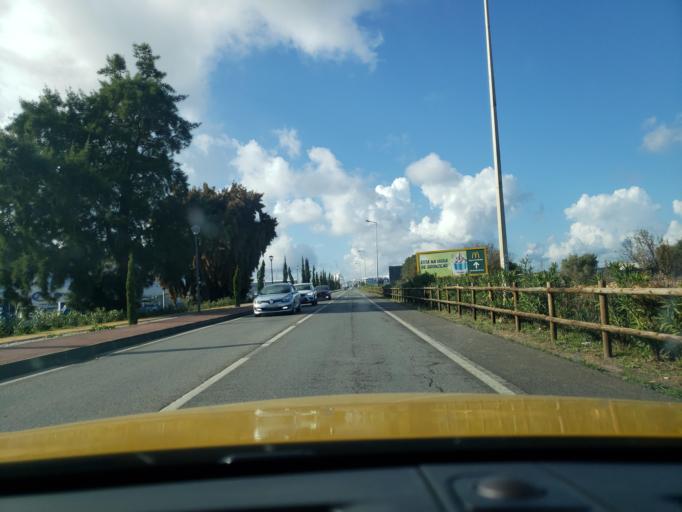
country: PT
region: Faro
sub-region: Portimao
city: Portimao
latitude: 37.1365
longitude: -8.5244
